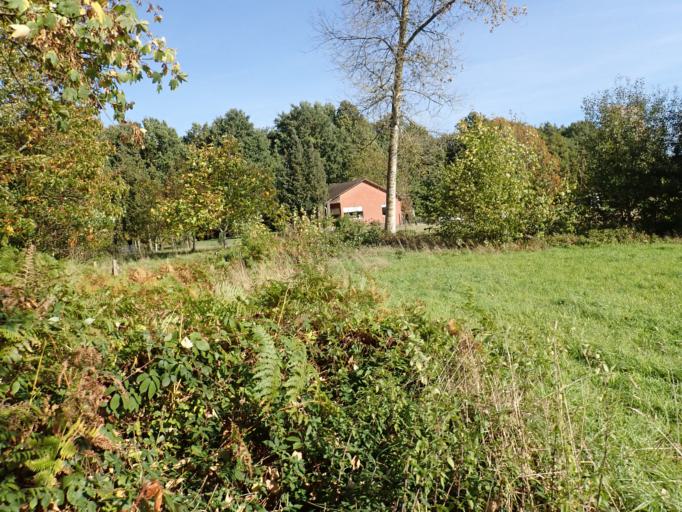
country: BE
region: Flanders
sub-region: Provincie Vlaams-Brabant
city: Holsbeek
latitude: 50.9374
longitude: 4.7449
